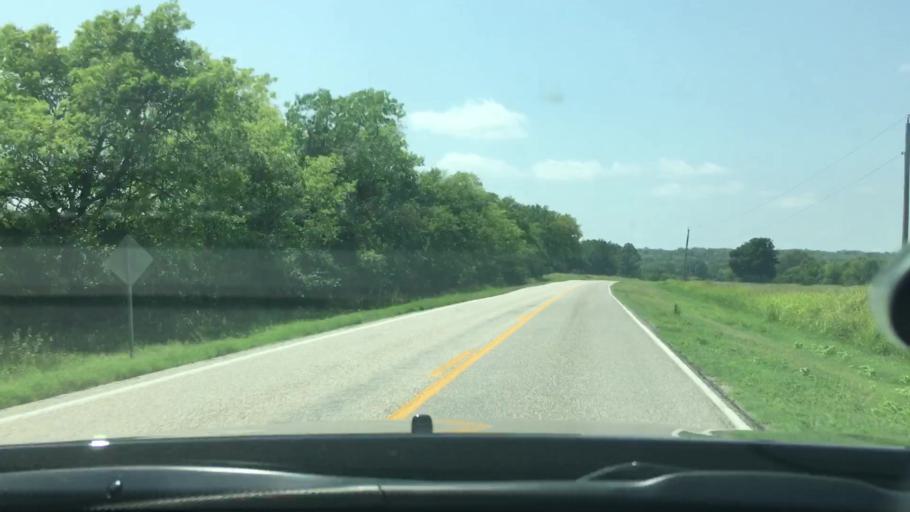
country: US
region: Oklahoma
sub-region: Johnston County
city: Tishomingo
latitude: 34.3749
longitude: -96.4443
